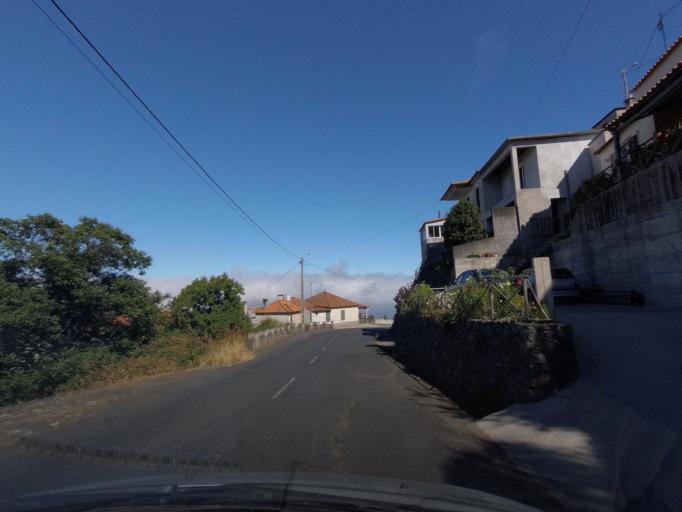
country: PT
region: Madeira
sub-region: Santa Cruz
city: Camacha
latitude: 32.6836
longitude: -16.8478
